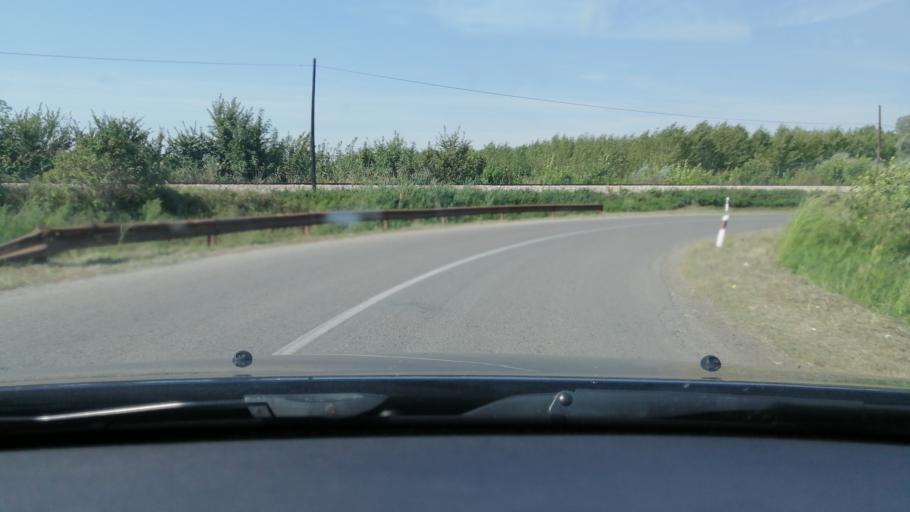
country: RS
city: Orlovat
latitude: 45.2477
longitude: 20.6046
